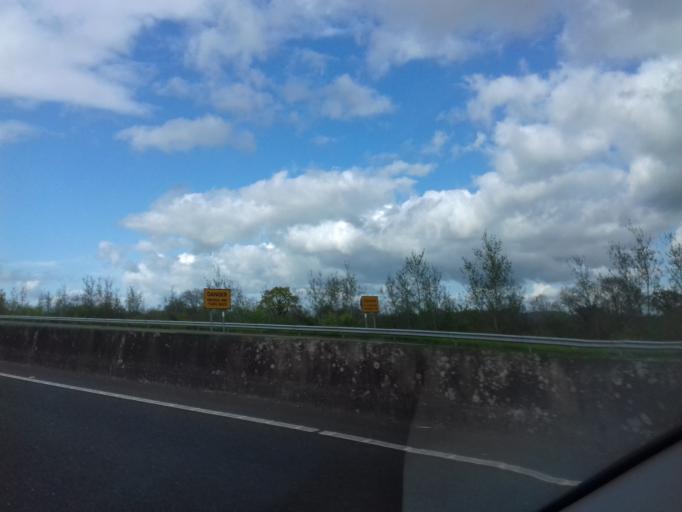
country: IE
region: Leinster
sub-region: Kilkenny
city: Thomastown
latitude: 52.4815
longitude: -7.2407
